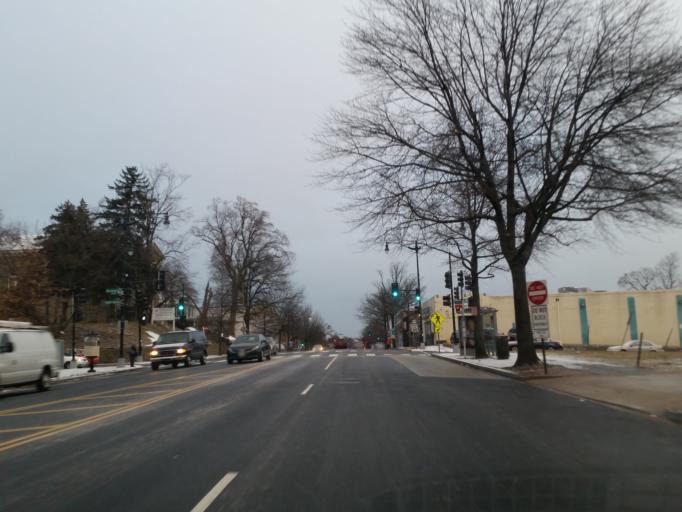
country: US
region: Maryland
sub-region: Montgomery County
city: Takoma Park
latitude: 38.9632
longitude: -77.0278
